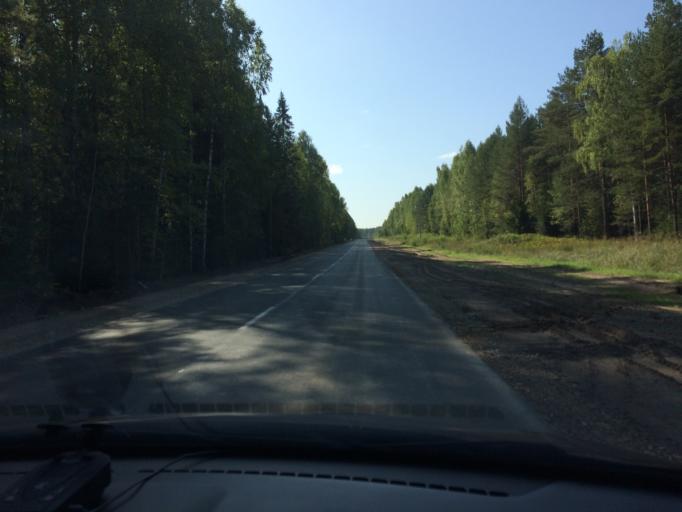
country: RU
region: Mariy-El
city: Sovetskiy
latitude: 56.5607
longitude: 48.4310
